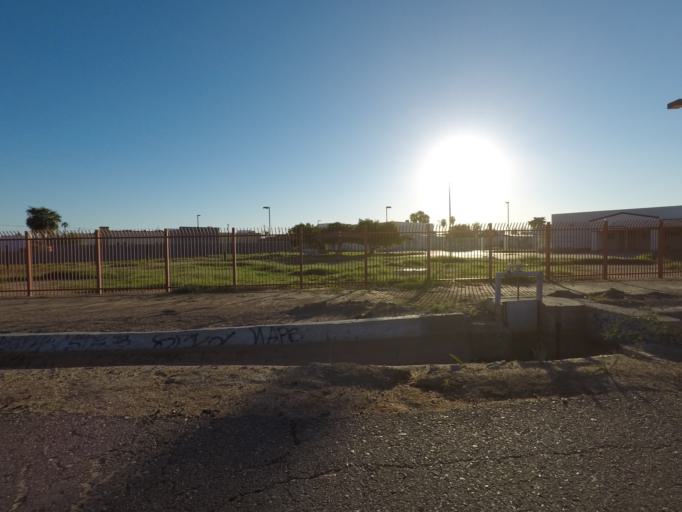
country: US
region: Arizona
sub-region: Maricopa County
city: Phoenix
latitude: 33.4675
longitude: -112.0186
